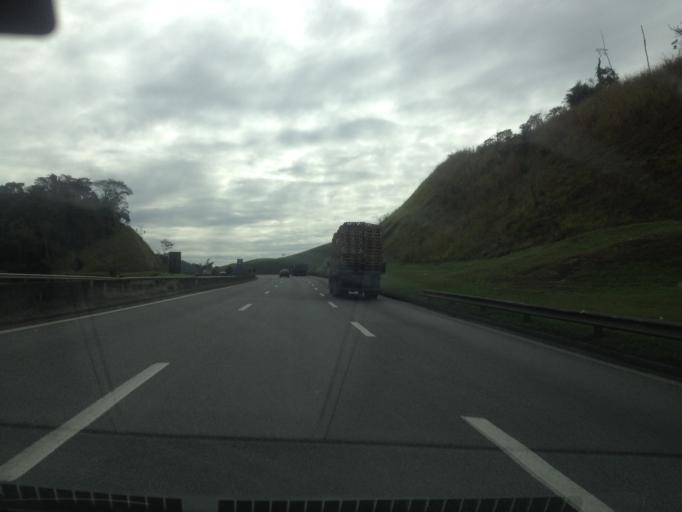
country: BR
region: Rio de Janeiro
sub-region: Pirai
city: Pirai
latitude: -22.6148
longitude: -43.9319
